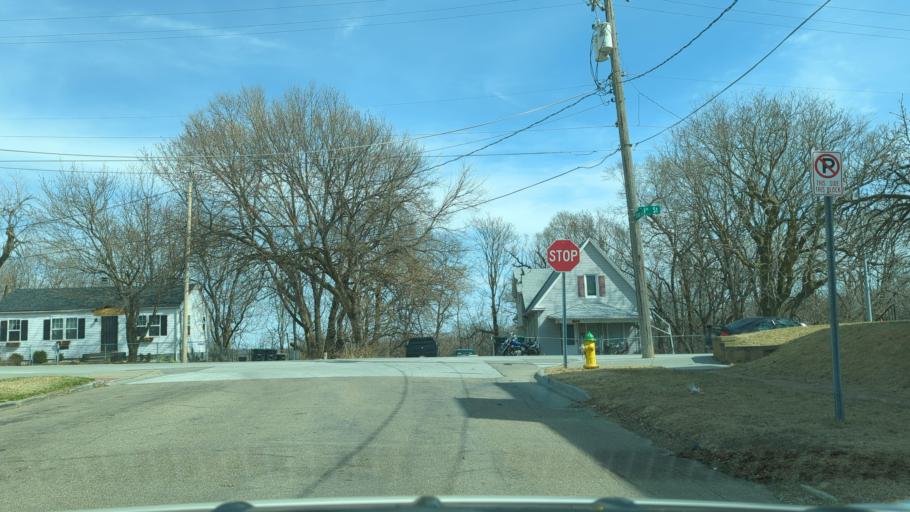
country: US
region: Nebraska
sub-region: Douglas County
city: Omaha
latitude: 41.2360
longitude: -95.9299
